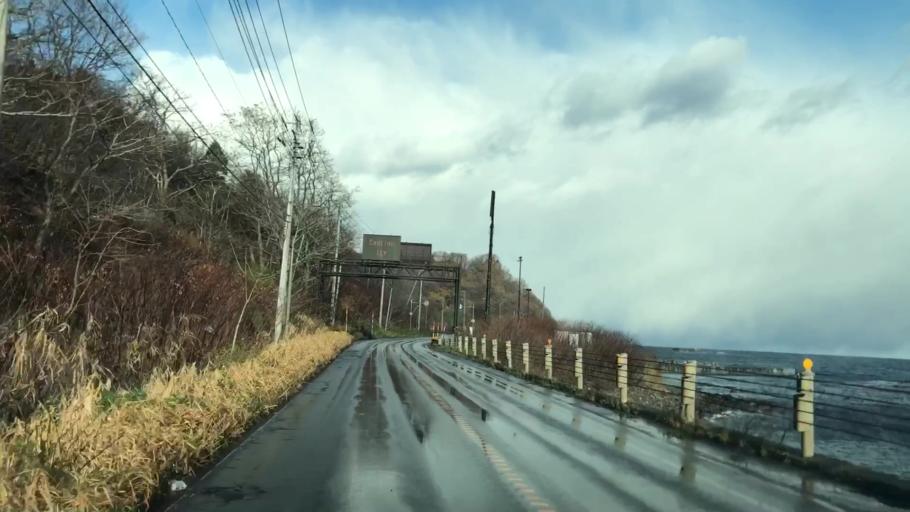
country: JP
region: Hokkaido
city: Yoichi
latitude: 43.2898
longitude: 140.6326
